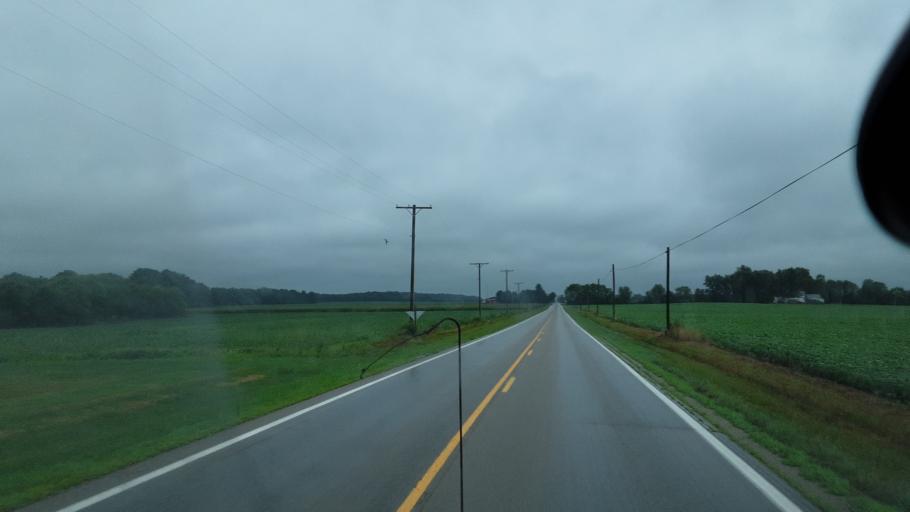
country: US
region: Ohio
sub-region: Mercer County
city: Rockford
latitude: 40.7426
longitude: -84.7458
